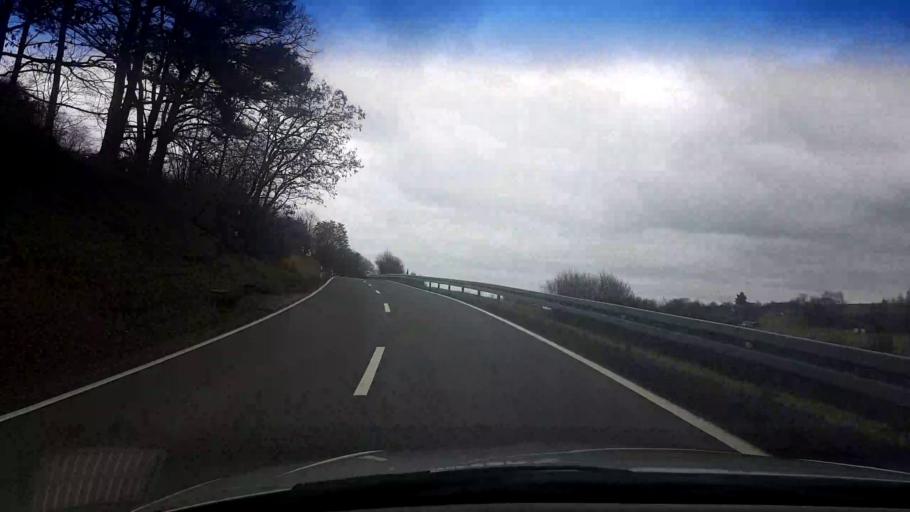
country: DE
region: Bavaria
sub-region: Regierungsbezirk Unterfranken
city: Eltmann
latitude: 49.9341
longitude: 10.6434
